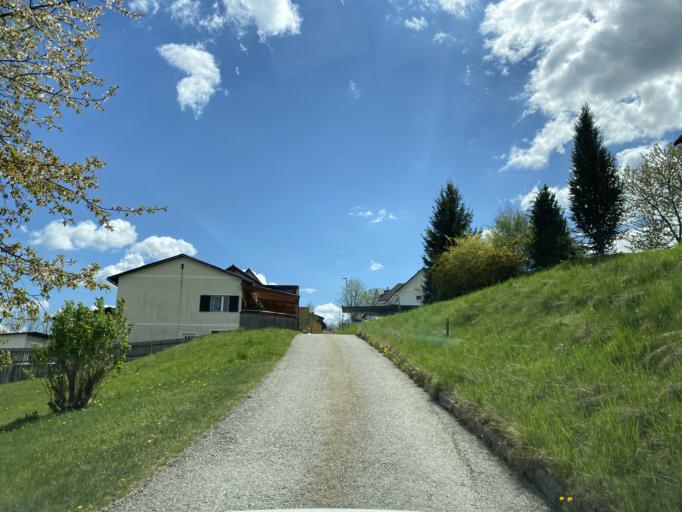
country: AT
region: Styria
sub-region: Politischer Bezirk Weiz
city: Birkfeld
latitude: 47.3561
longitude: 15.6896
